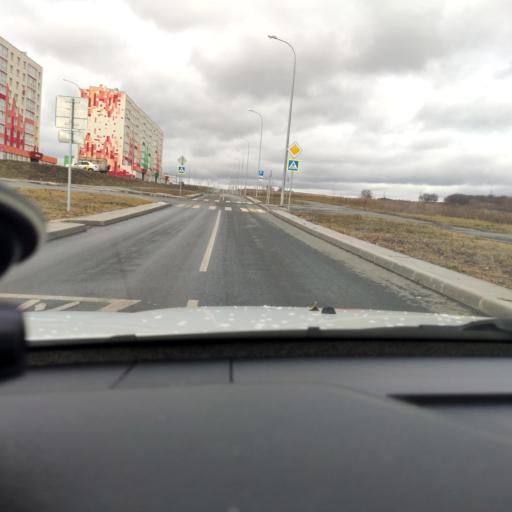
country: RU
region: Samara
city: Petra-Dubrava
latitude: 53.3005
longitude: 50.3296
